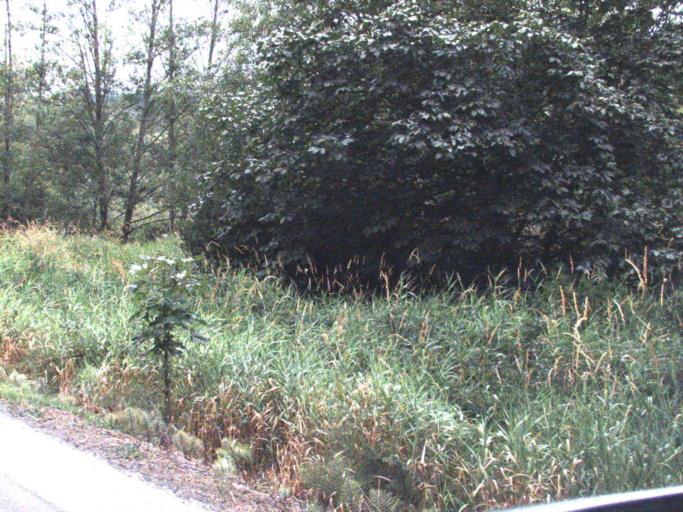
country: US
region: Washington
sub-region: King County
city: Fall City
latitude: 47.5770
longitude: -121.8920
